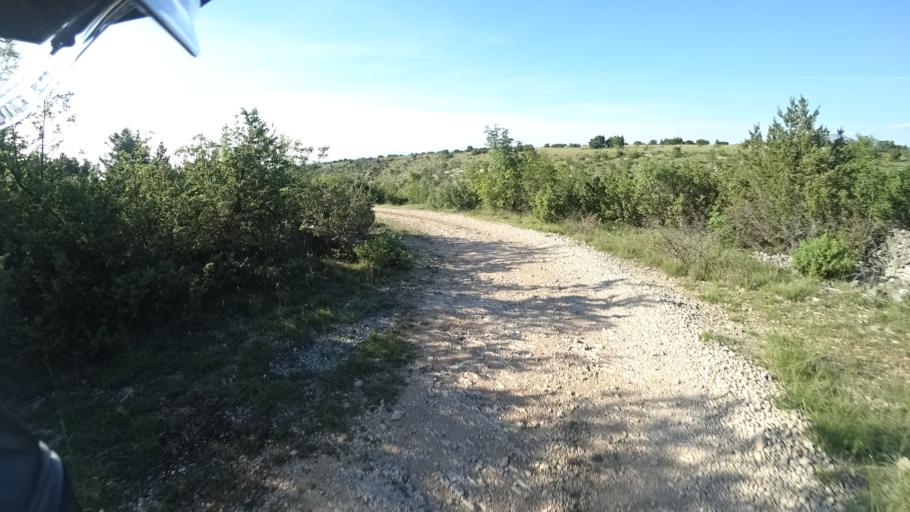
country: HR
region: Sibensko-Kniniska
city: Drnis
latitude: 43.8135
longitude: 16.0281
